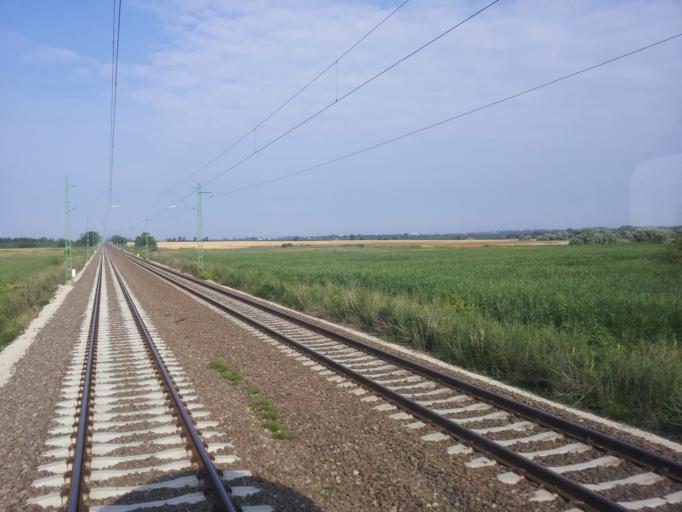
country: HU
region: Fejer
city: Pakozd
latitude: 47.1755
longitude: 18.5332
